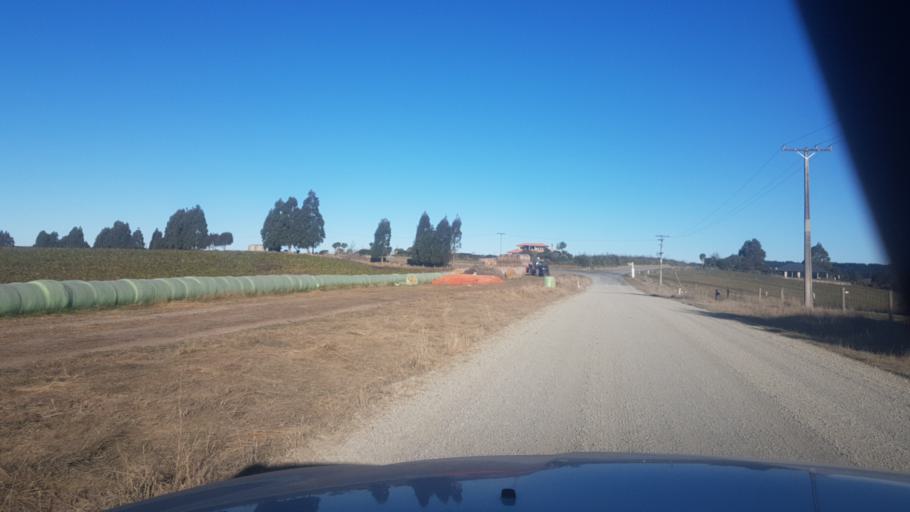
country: NZ
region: Canterbury
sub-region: Timaru District
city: Pleasant Point
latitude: -44.3583
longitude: 171.0695
